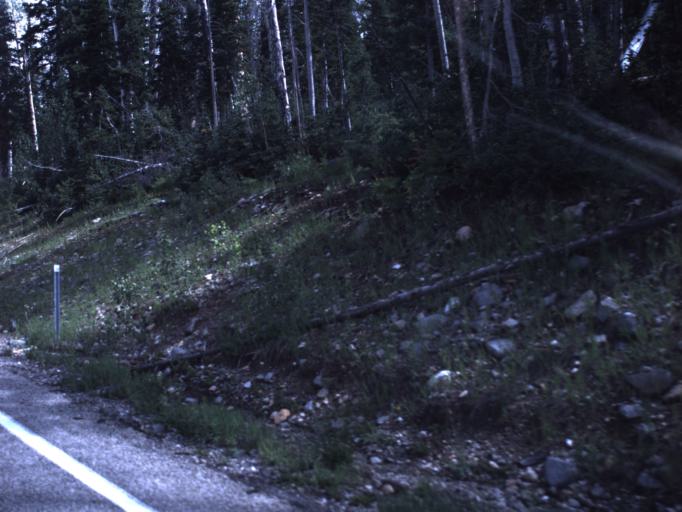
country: US
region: Utah
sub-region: Iron County
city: Cedar City
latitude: 37.5776
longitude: -112.8423
